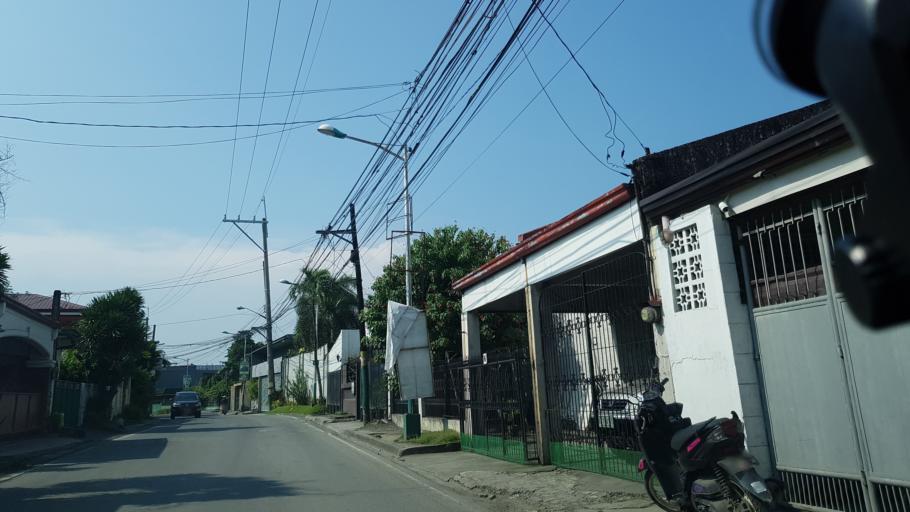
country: PH
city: Sambayanihan People's Village
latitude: 14.4982
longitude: 121.0128
